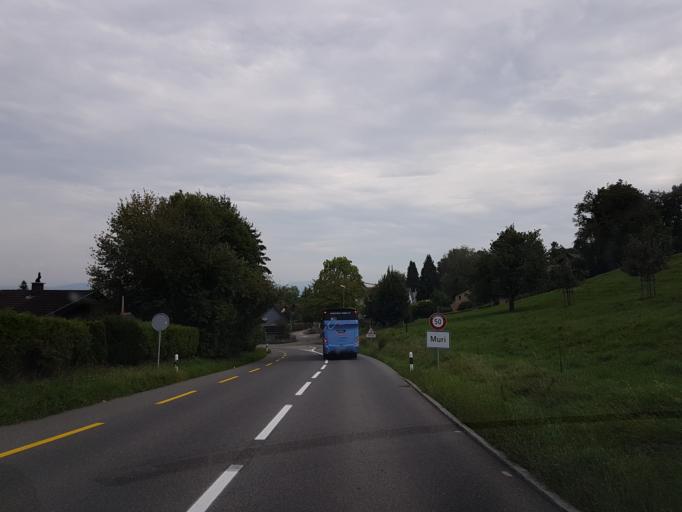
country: CH
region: Aargau
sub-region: Bezirk Muri
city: Muri
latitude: 47.2726
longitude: 8.3309
